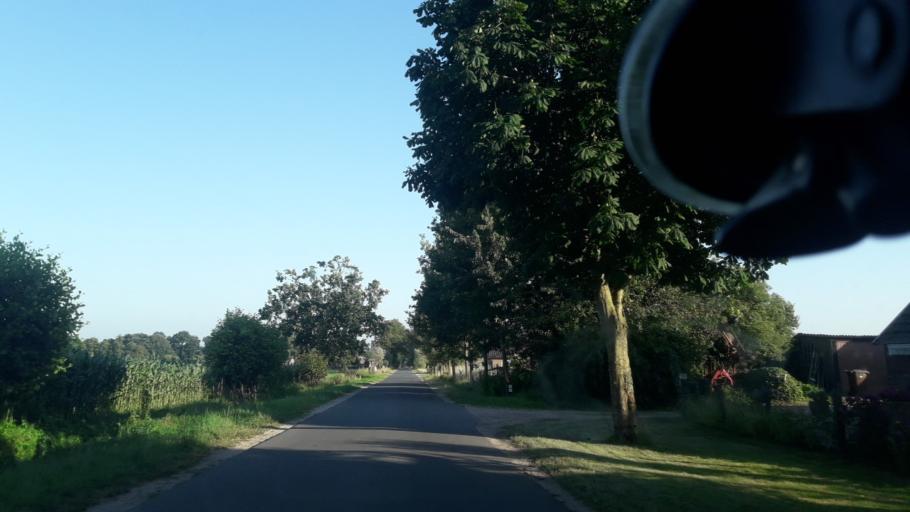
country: NL
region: Gelderland
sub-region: Gemeente Ede
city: Ede
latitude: 52.0105
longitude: 5.6141
